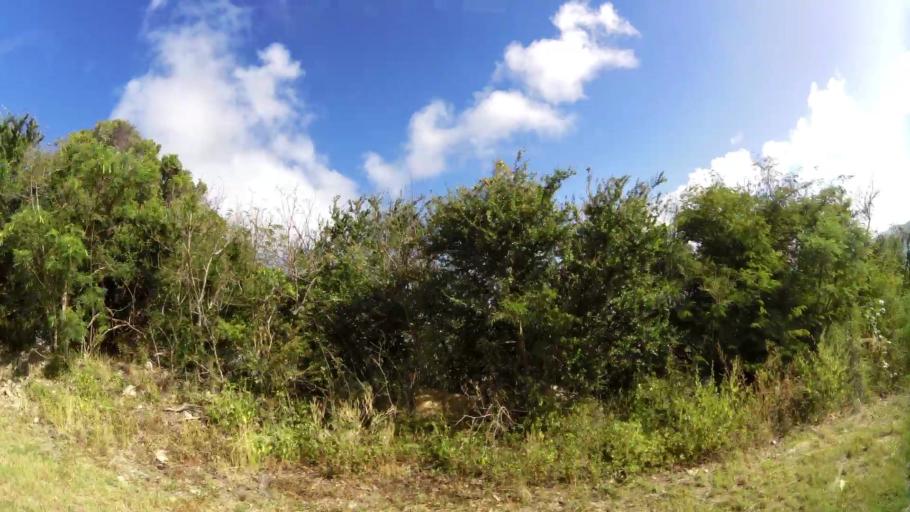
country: VG
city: Tortola
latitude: 18.4327
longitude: -64.5776
